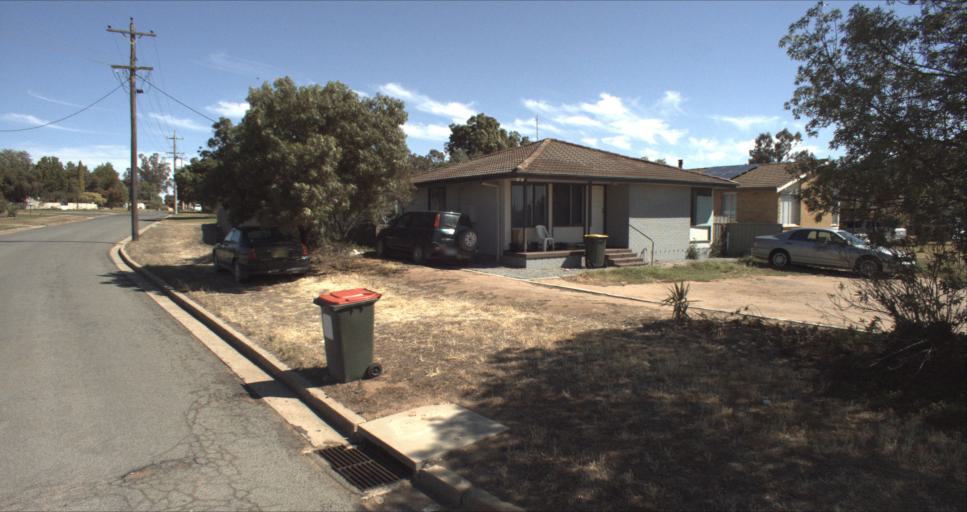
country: AU
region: New South Wales
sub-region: Leeton
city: Leeton
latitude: -34.5483
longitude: 146.3744
